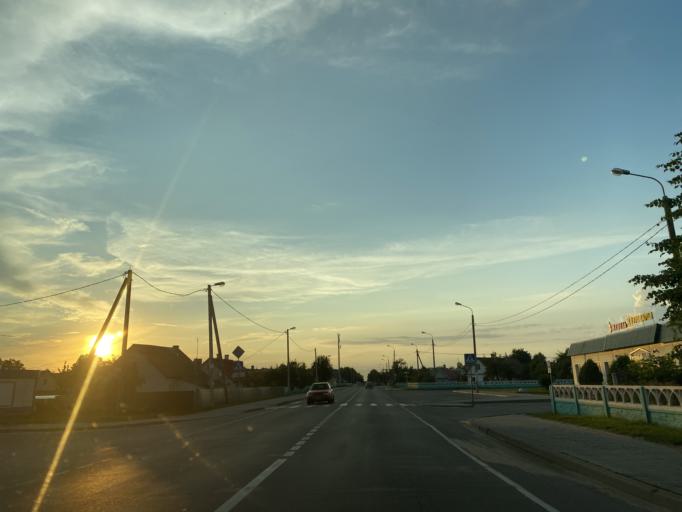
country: BY
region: Brest
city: Ivatsevichy
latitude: 52.7094
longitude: 25.3537
